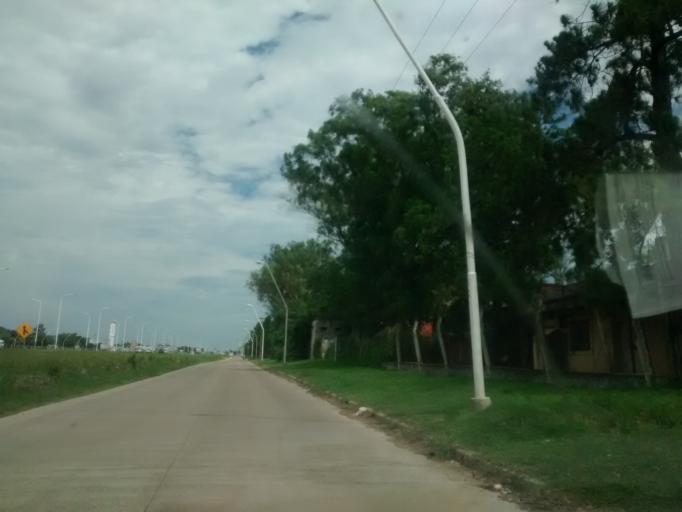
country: AR
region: Chaco
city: Fontana
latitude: -27.4111
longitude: -58.9771
